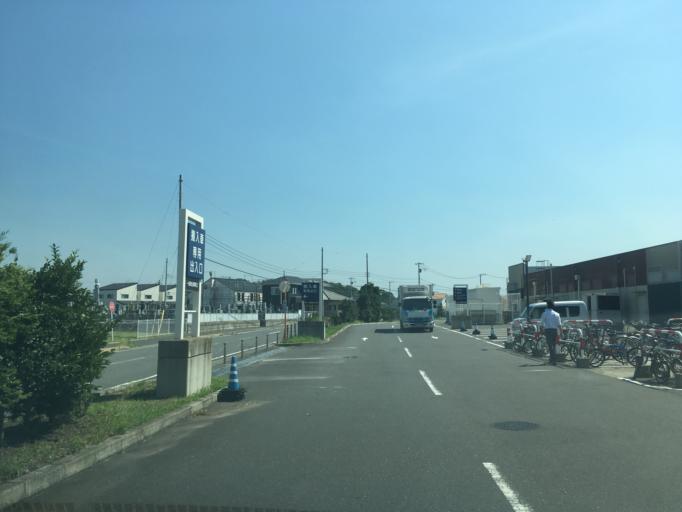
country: JP
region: Chiba
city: Kisarazu
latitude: 35.4354
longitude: 139.9365
